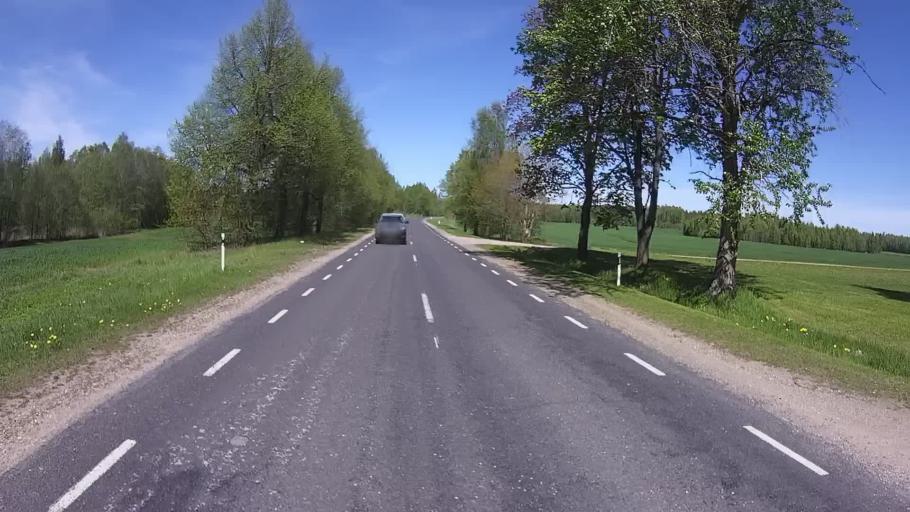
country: EE
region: Polvamaa
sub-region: Raepina vald
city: Rapina
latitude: 58.0453
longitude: 27.3889
